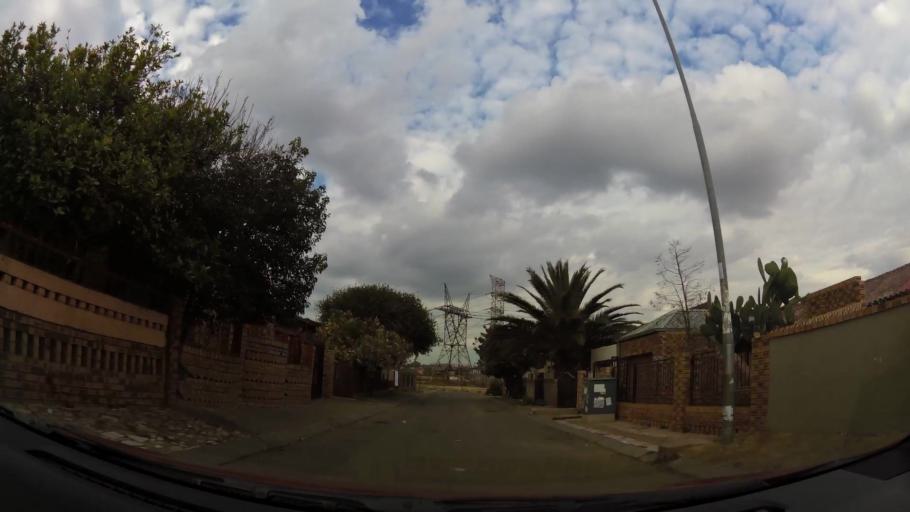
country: ZA
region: Gauteng
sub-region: City of Johannesburg Metropolitan Municipality
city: Soweto
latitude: -26.2481
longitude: 27.8367
